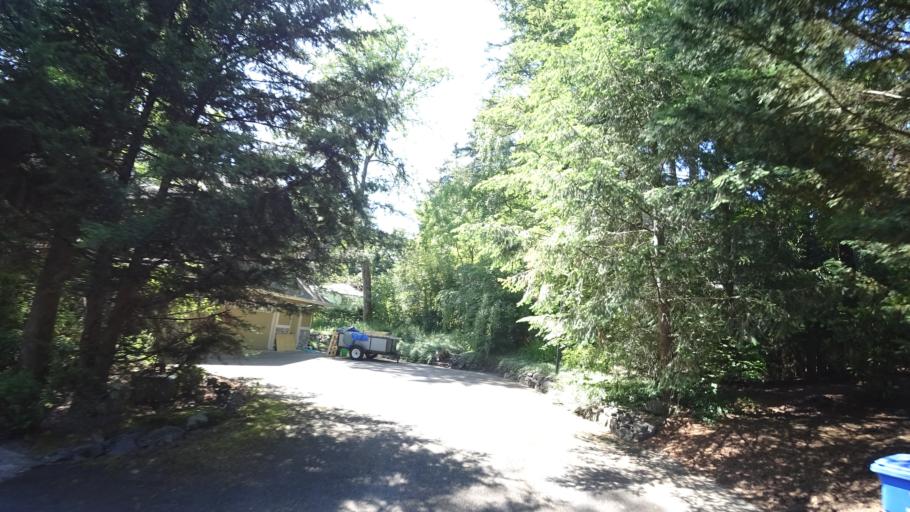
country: US
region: Oregon
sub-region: Washington County
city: Metzger
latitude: 45.4461
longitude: -122.7195
